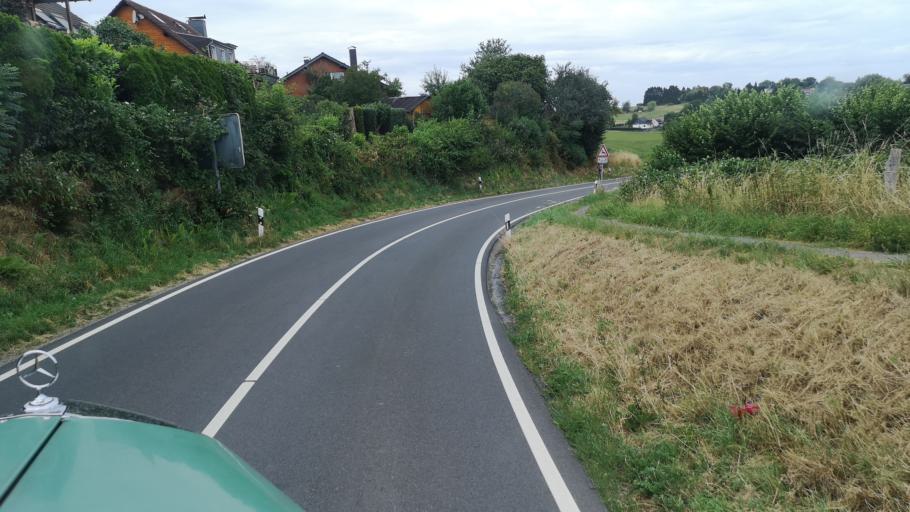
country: DE
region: North Rhine-Westphalia
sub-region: Regierungsbezirk Koln
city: Odenthal
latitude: 51.0533
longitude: 7.1752
